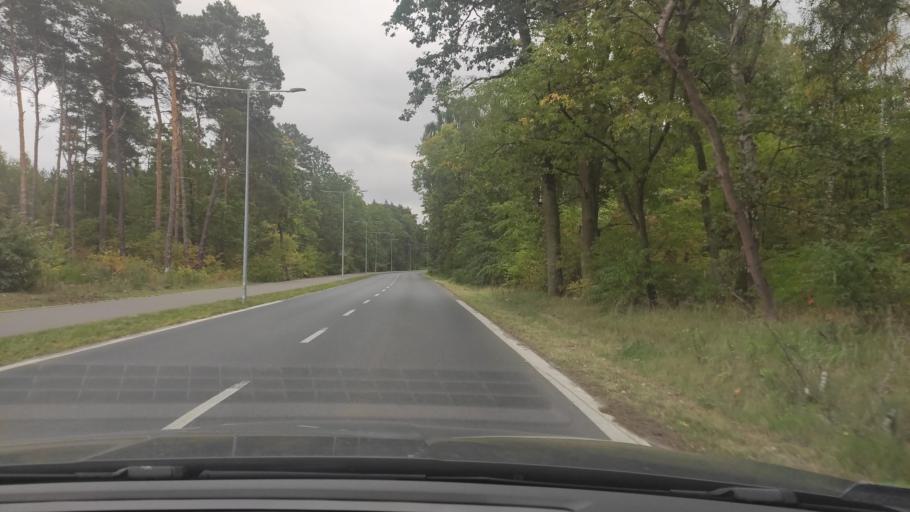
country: PL
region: Greater Poland Voivodeship
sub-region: Powiat poznanski
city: Swarzedz
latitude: 52.3874
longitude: 17.0488
